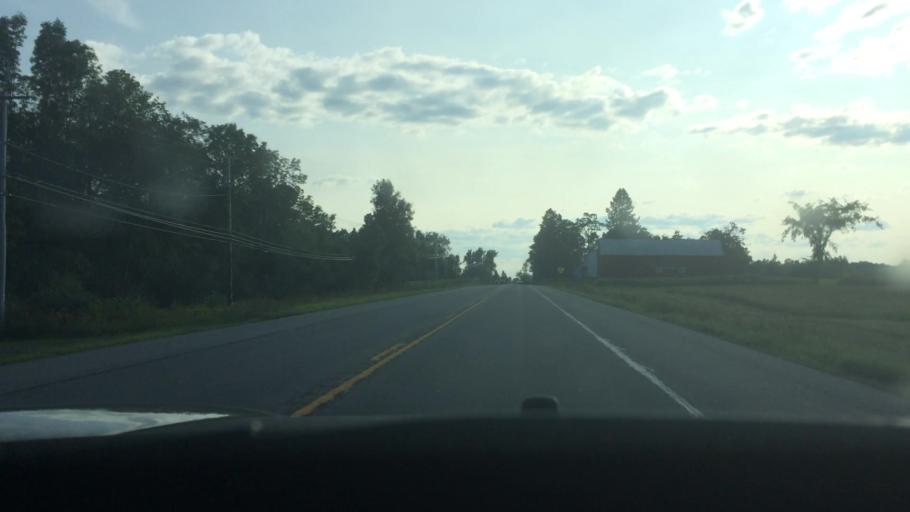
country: US
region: New York
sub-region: St. Lawrence County
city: Potsdam
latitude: 44.6394
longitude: -75.0689
